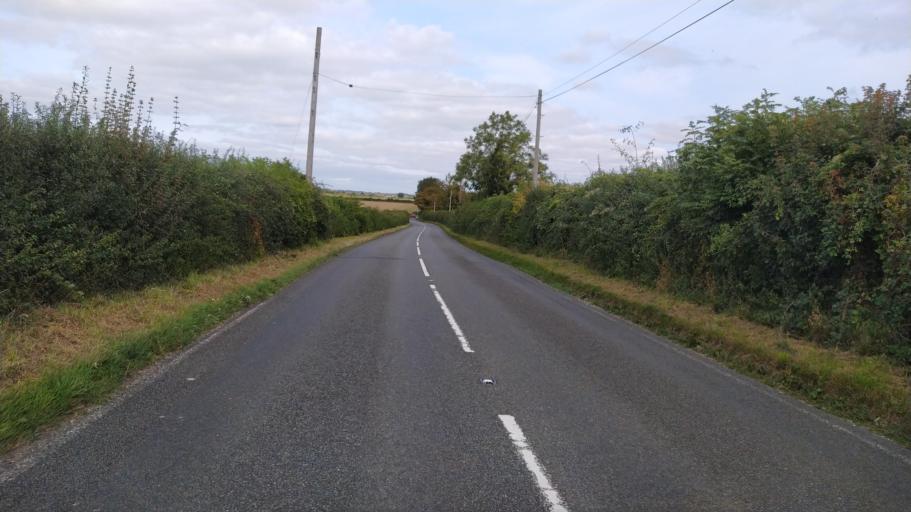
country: GB
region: England
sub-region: Dorset
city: Three Legged Cross
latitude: 50.8797
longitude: -1.9746
